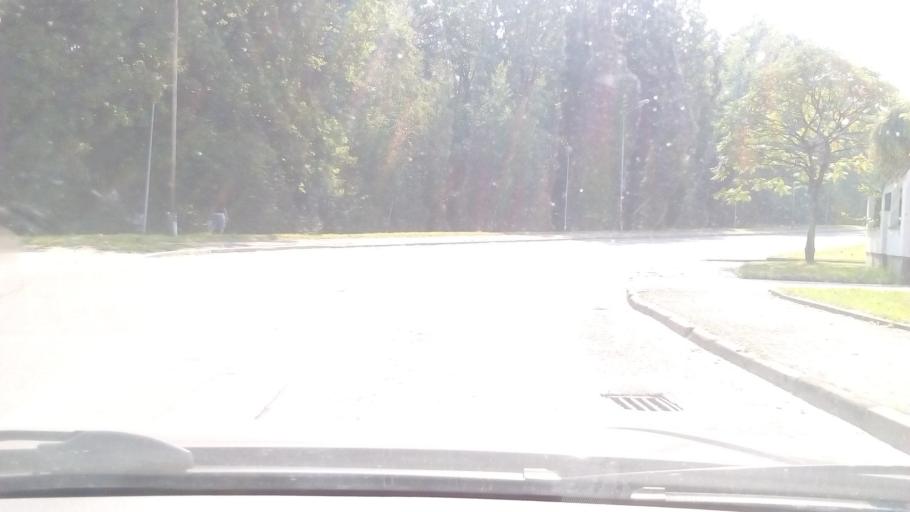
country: LT
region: Alytaus apskritis
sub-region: Alytus
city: Alytus
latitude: 54.3874
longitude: 24.0630
